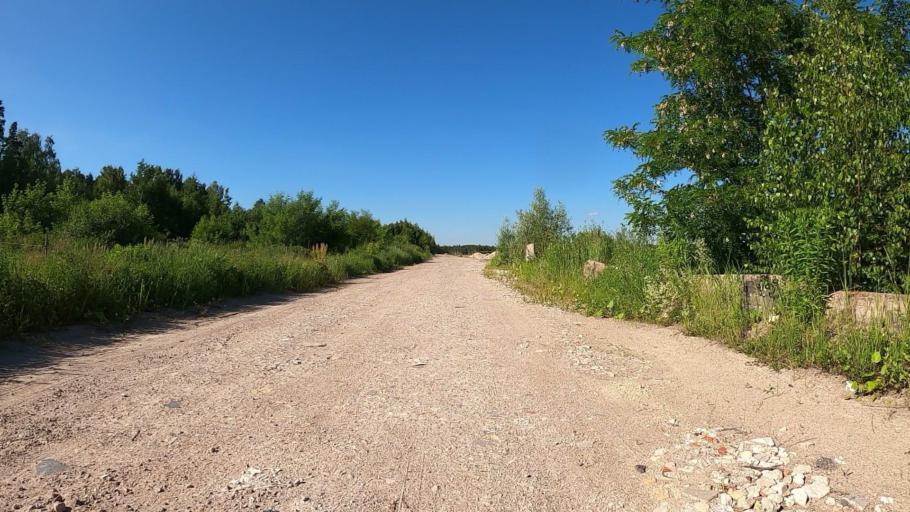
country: LV
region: Stopini
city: Ulbroka
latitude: 56.8797
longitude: 24.2776
